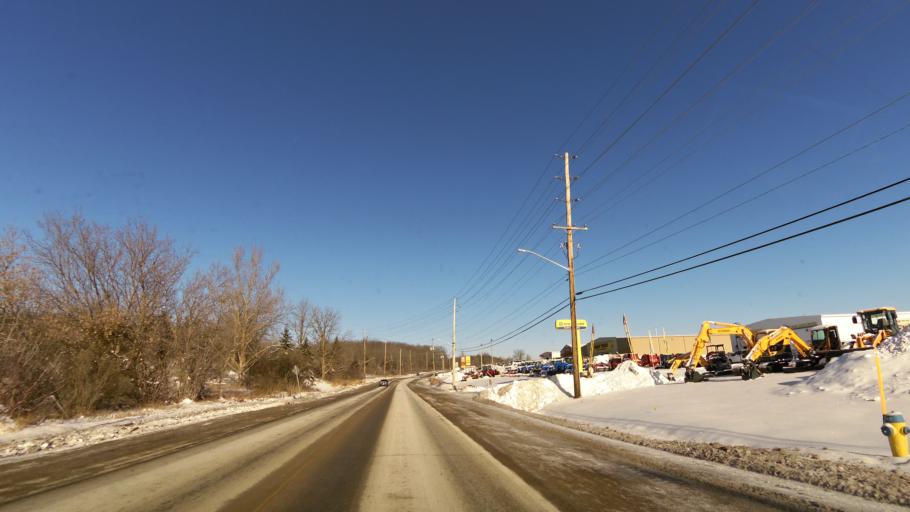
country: CA
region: Ontario
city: Quinte West
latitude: 44.2844
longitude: -77.8095
